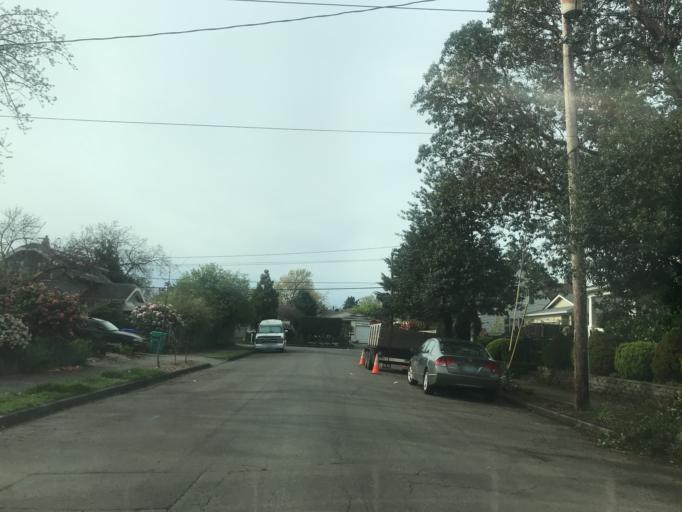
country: US
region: Oregon
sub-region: Multnomah County
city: Lents
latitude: 45.4945
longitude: -122.5932
